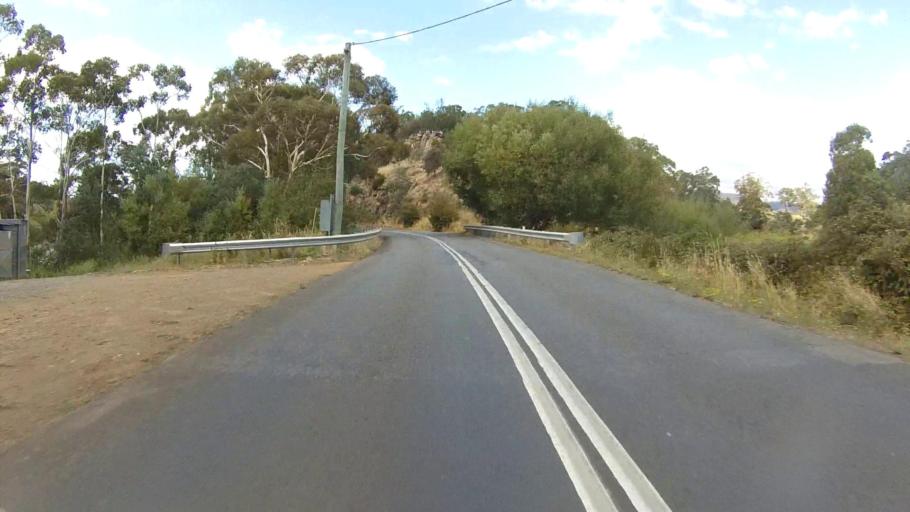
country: AU
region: Tasmania
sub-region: Derwent Valley
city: New Norfolk
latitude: -42.7574
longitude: 146.9867
